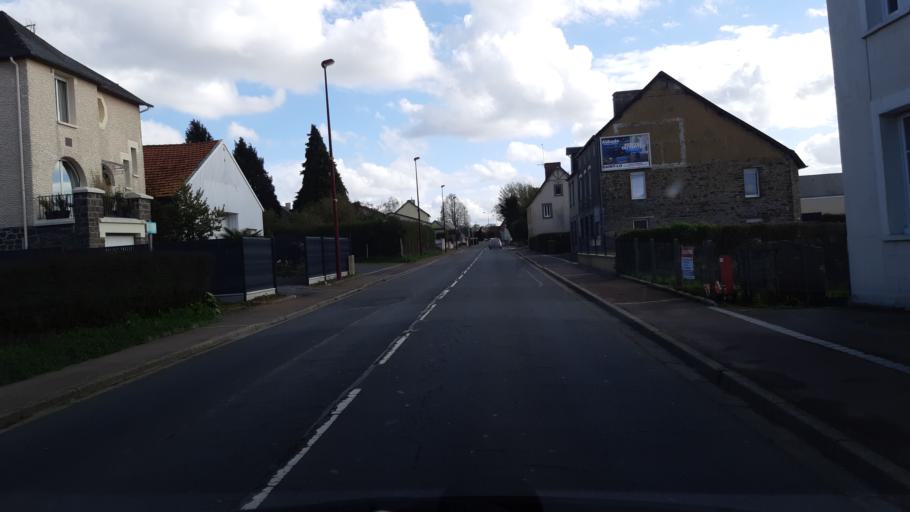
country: FR
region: Lower Normandy
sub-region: Departement de la Manche
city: Agneaux
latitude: 49.0478
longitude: -1.1283
